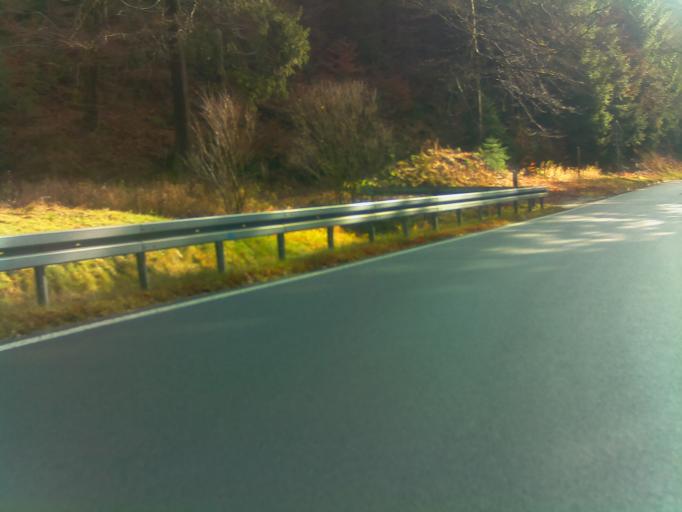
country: DE
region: Thuringia
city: Masserberg
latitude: 50.5386
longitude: 10.9674
